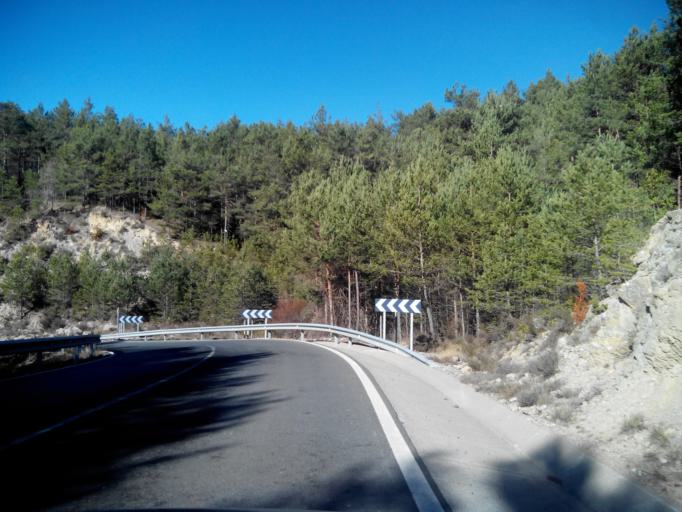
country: ES
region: Catalonia
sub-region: Provincia de Barcelona
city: Capolat
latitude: 42.1198
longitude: 1.6873
